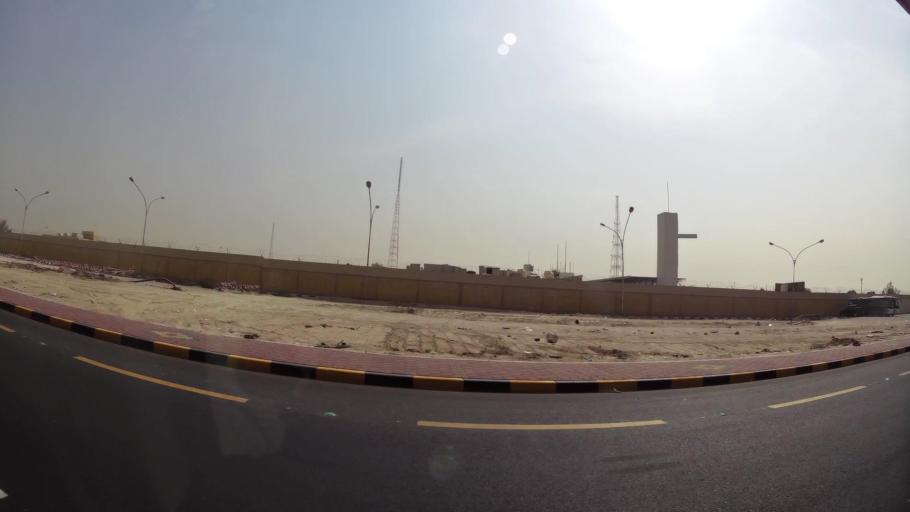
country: KW
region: Al Asimah
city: Ar Rabiyah
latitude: 29.3221
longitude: 47.9111
